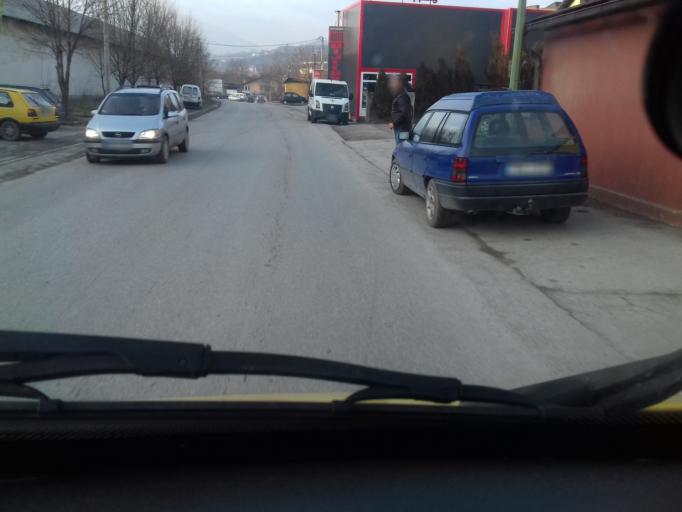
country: BA
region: Federation of Bosnia and Herzegovina
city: Kakanj
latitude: 44.1237
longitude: 18.1042
